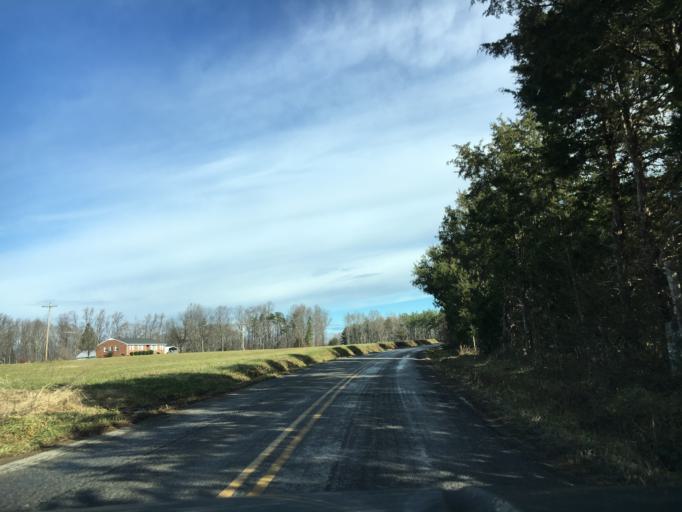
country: US
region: Virginia
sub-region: Nottoway County
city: Crewe
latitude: 37.3225
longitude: -78.1734
